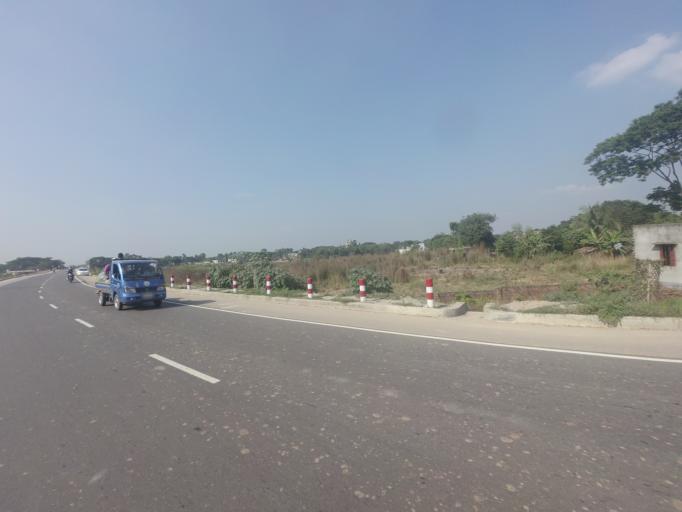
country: BD
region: Dhaka
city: Azimpur
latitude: 23.7336
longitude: 90.3337
